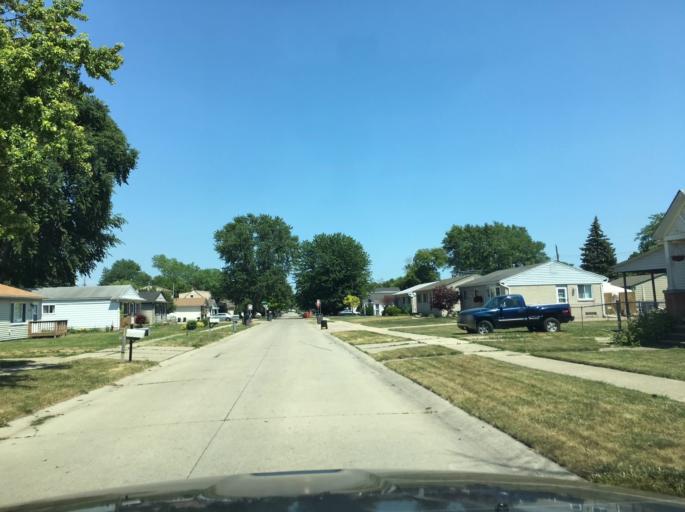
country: US
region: Michigan
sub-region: Macomb County
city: Fraser
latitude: 42.5427
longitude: -82.9146
